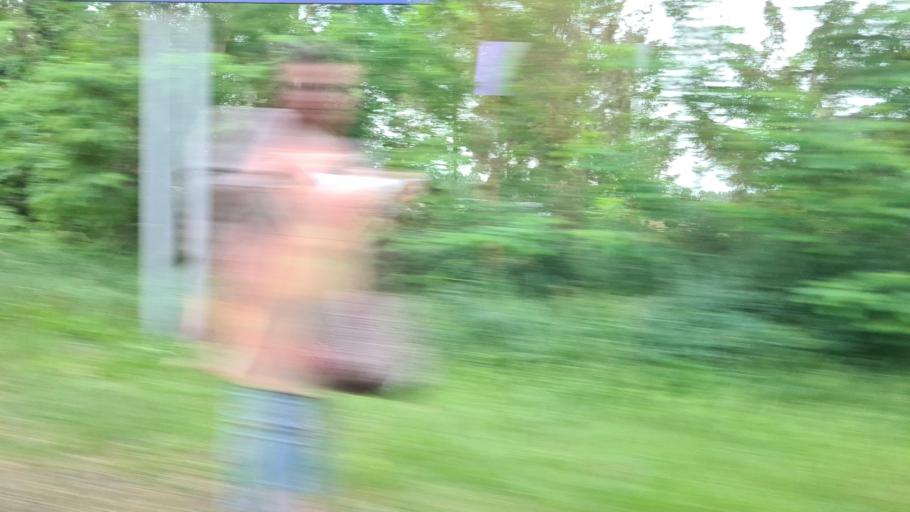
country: DE
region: Brandenburg
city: Schonborn
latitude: 51.6021
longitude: 13.4671
